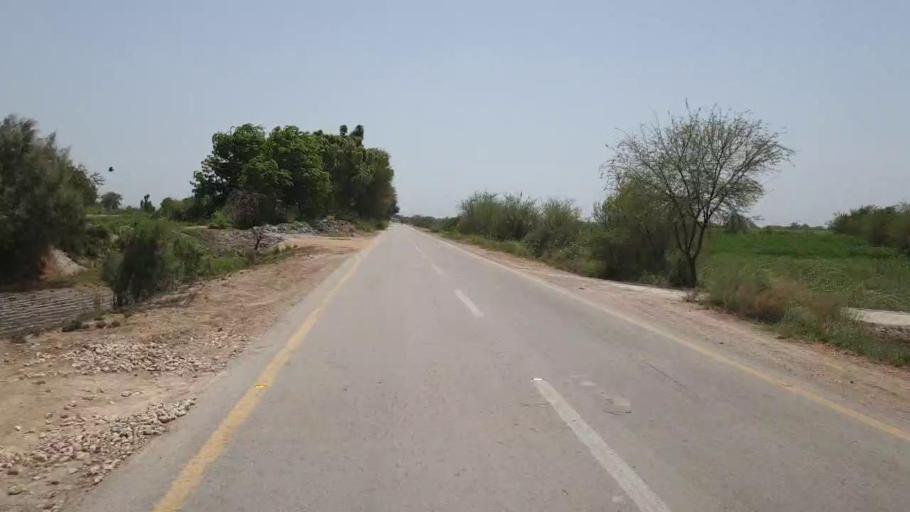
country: PK
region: Sindh
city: Daur
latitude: 26.3520
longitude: 68.1434
